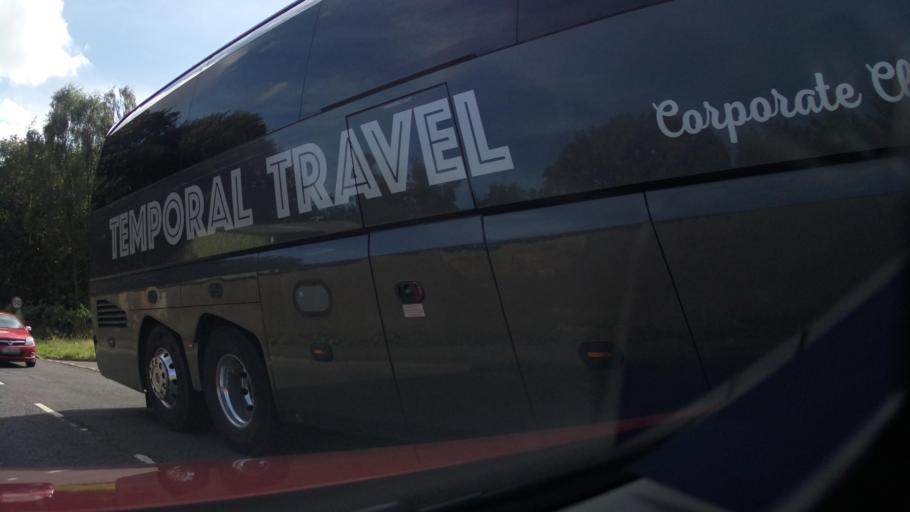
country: GB
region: Scotland
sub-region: Stirling
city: Cowie
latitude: 56.0394
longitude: -3.8592
